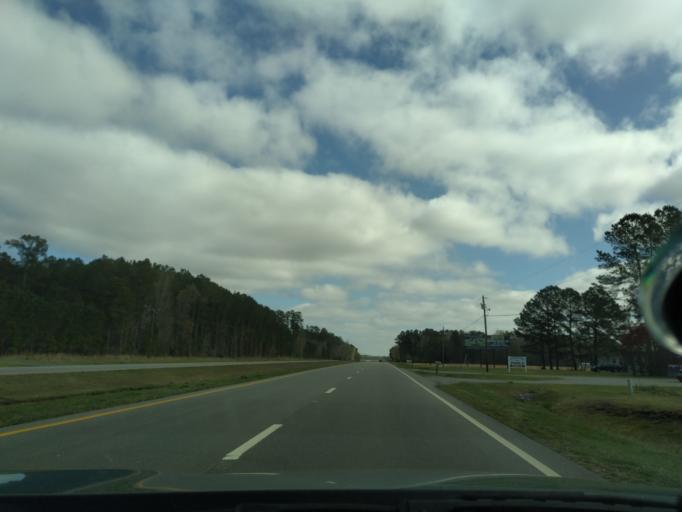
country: US
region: North Carolina
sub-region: Perquimans County
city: Hertford
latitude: 36.1221
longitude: -76.5064
